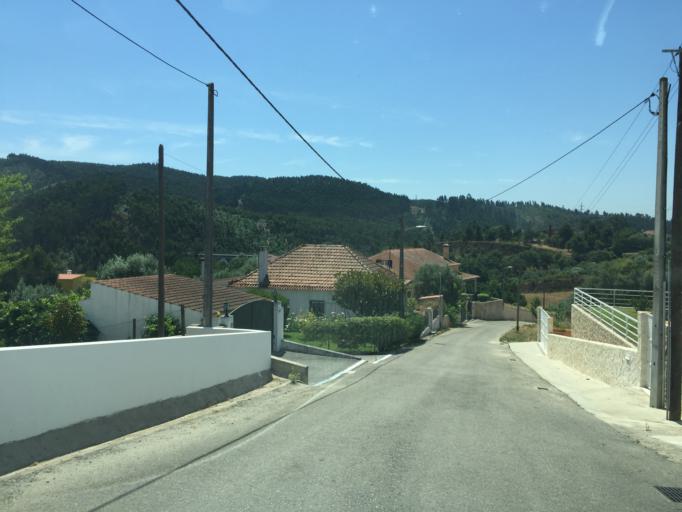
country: PT
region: Santarem
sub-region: Tomar
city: Tomar
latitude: 39.5948
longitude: -8.3482
